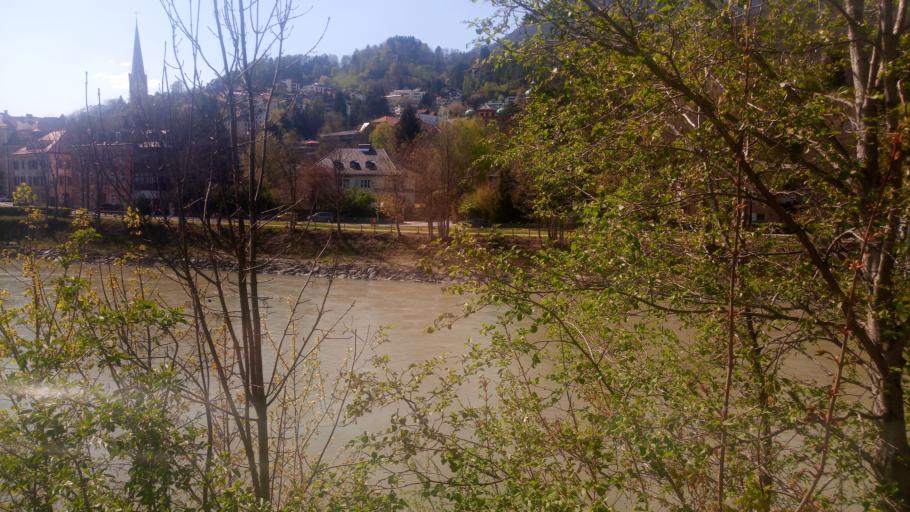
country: AT
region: Tyrol
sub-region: Innsbruck Stadt
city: Innsbruck
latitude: 47.2767
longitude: 11.3972
